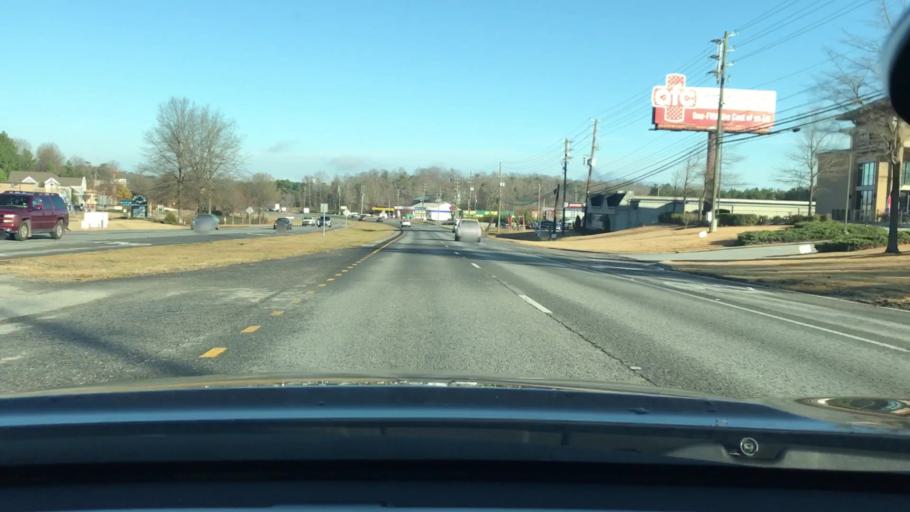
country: US
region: Alabama
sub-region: Shelby County
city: Lake Purdy
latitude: 33.4111
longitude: -86.6646
